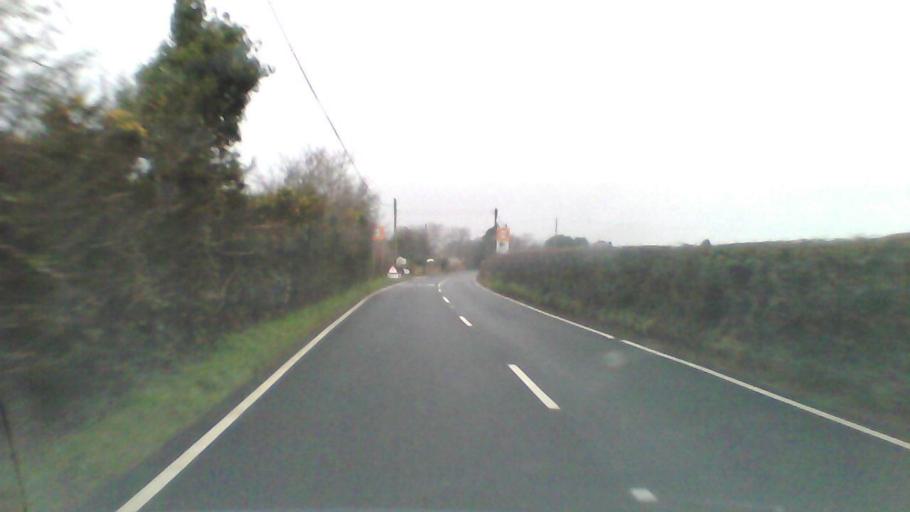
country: GB
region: England
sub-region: Isle of Wight
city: Newport
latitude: 50.6981
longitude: -1.2680
